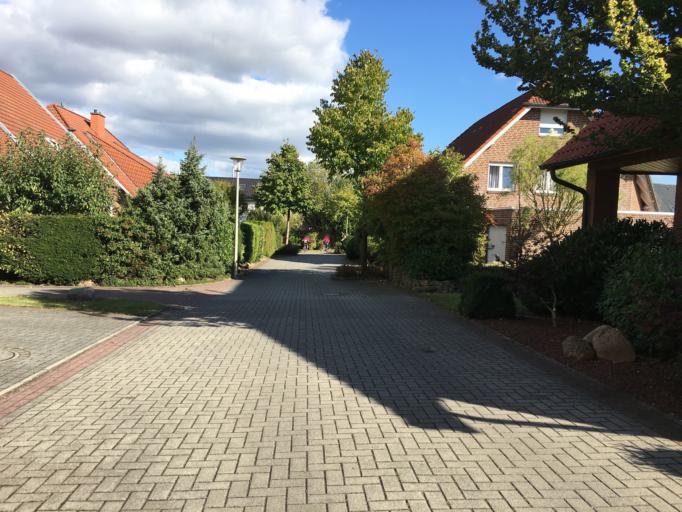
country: DE
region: North Rhine-Westphalia
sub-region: Regierungsbezirk Munster
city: Steinfurt
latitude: 52.1452
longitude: 7.3272
